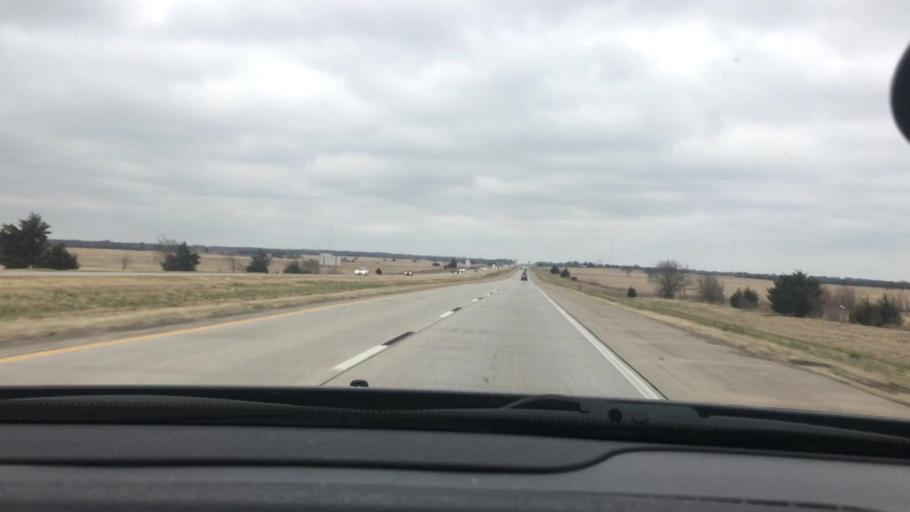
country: US
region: Oklahoma
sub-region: Bryan County
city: Durant
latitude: 34.1438
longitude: -96.2660
